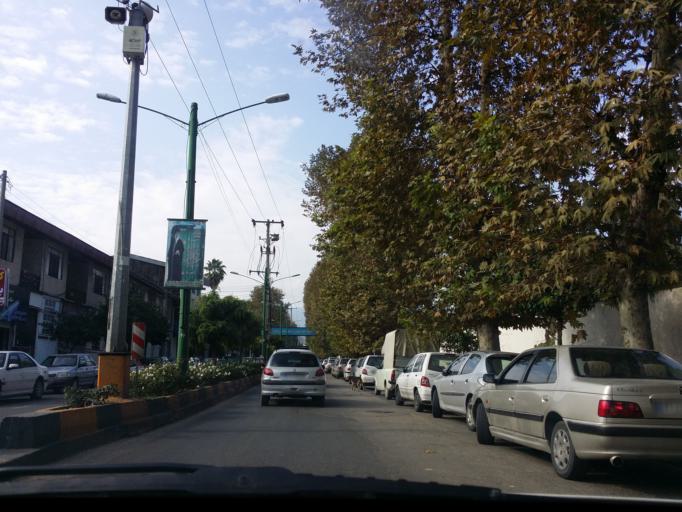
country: IR
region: Mazandaran
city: Chalus
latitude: 36.6505
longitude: 51.4214
